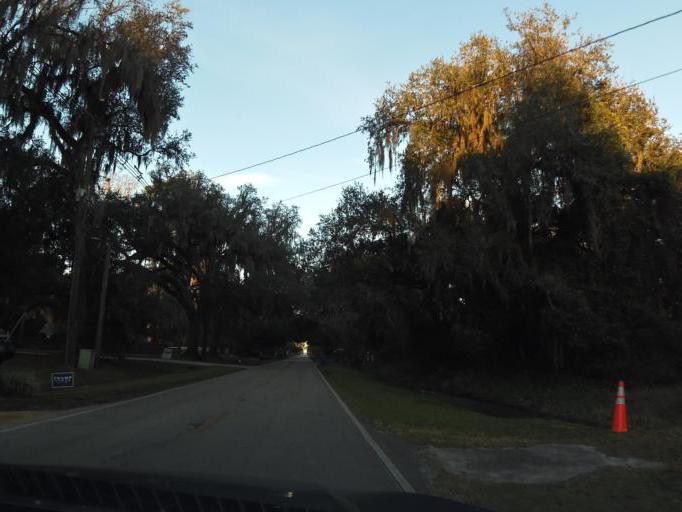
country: US
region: Florida
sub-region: Clay County
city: Green Cove Springs
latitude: 29.9327
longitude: -81.5713
